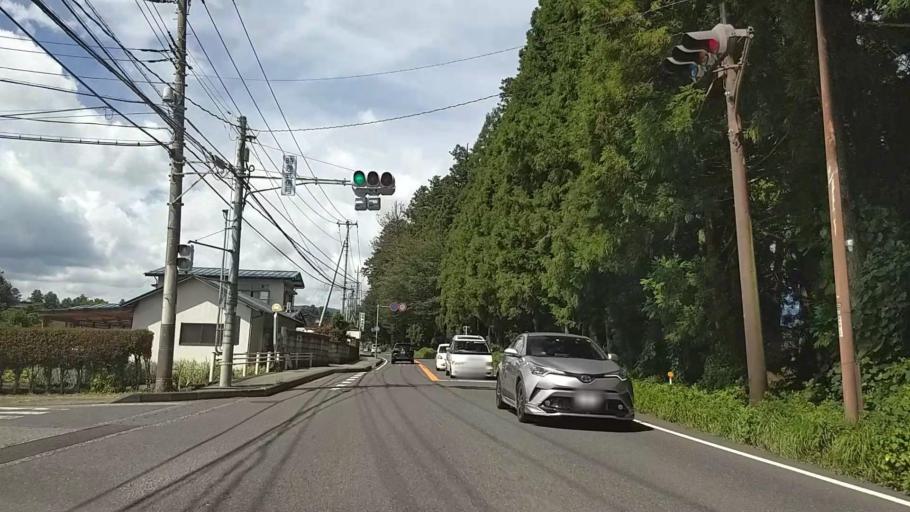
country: JP
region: Tochigi
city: Imaichi
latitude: 36.7213
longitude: 139.6981
